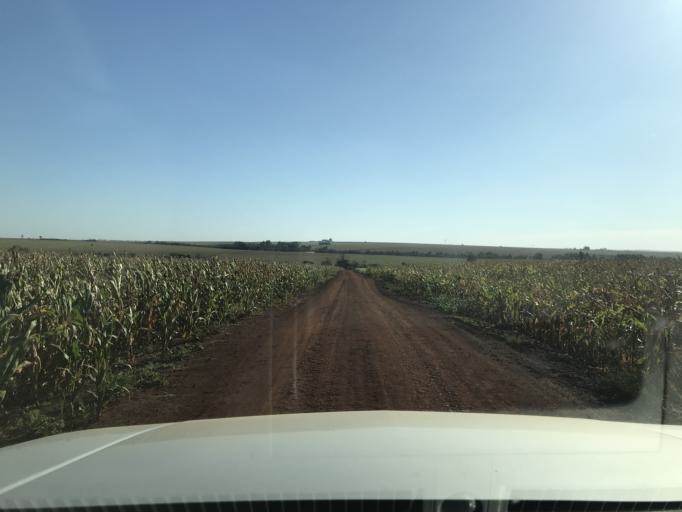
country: BR
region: Parana
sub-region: Palotina
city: Palotina
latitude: -24.2274
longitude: -53.8072
